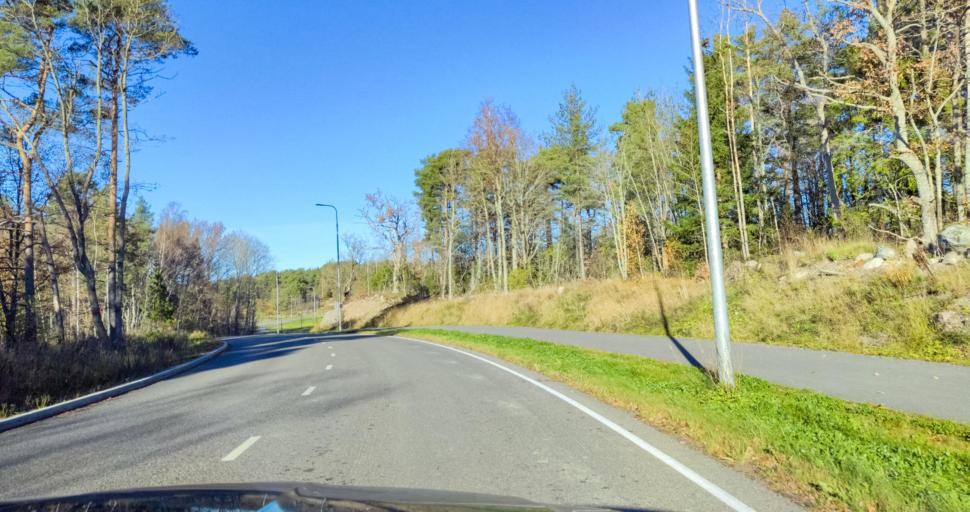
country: FI
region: Varsinais-Suomi
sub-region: Turku
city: Turku
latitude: 60.4088
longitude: 22.2106
